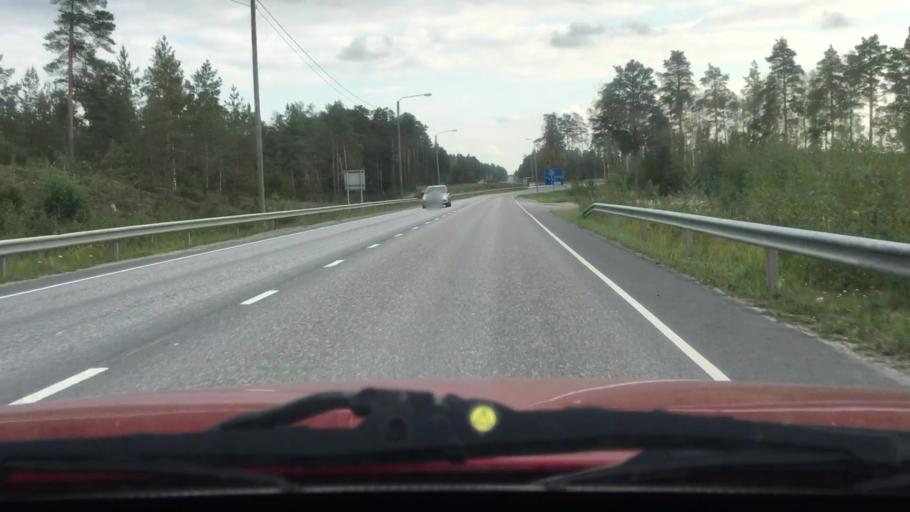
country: FI
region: Varsinais-Suomi
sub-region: Turku
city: Masku
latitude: 60.5451
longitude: 22.1281
